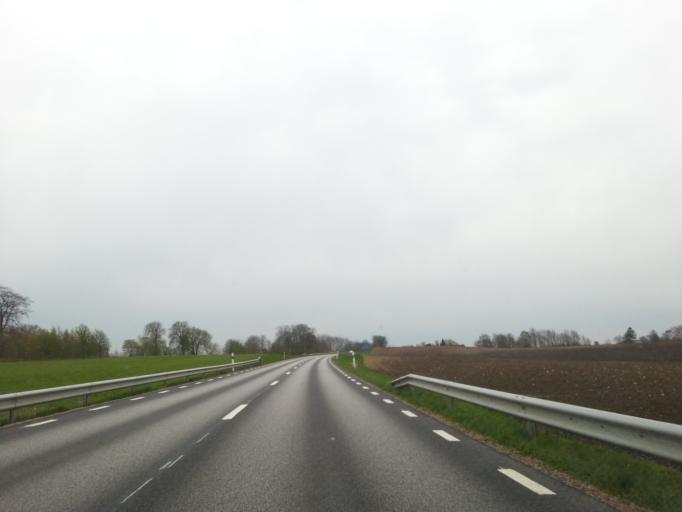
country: SE
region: Skane
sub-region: Svedala Kommun
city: Klagerup
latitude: 55.6047
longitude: 13.2658
